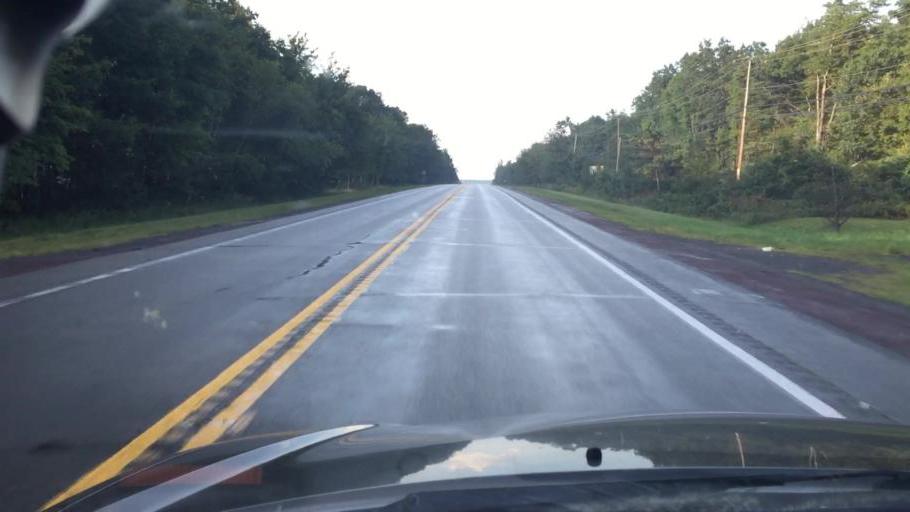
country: US
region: Pennsylvania
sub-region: Carbon County
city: Towamensing Trails
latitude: 40.9406
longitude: -75.6553
